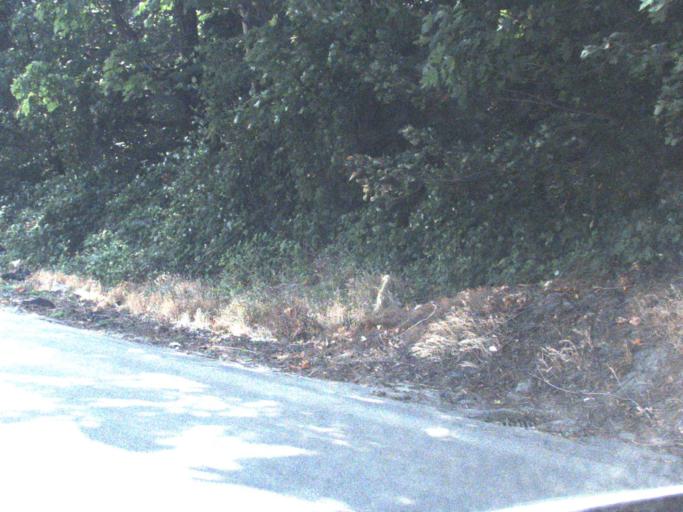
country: US
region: Washington
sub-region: King County
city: West Lake Sammamish
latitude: 47.5731
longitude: -122.1184
